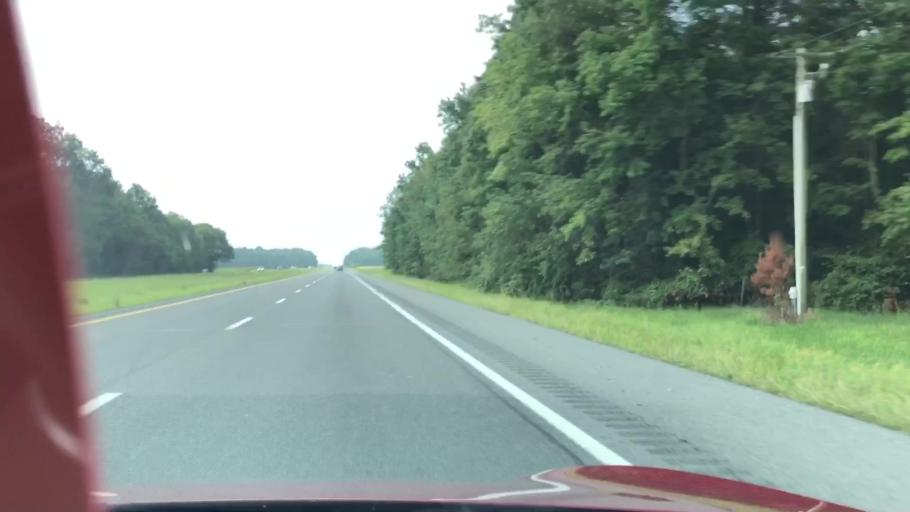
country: US
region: Delaware
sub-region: Sussex County
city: Laurel
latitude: 38.5181
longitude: -75.5572
